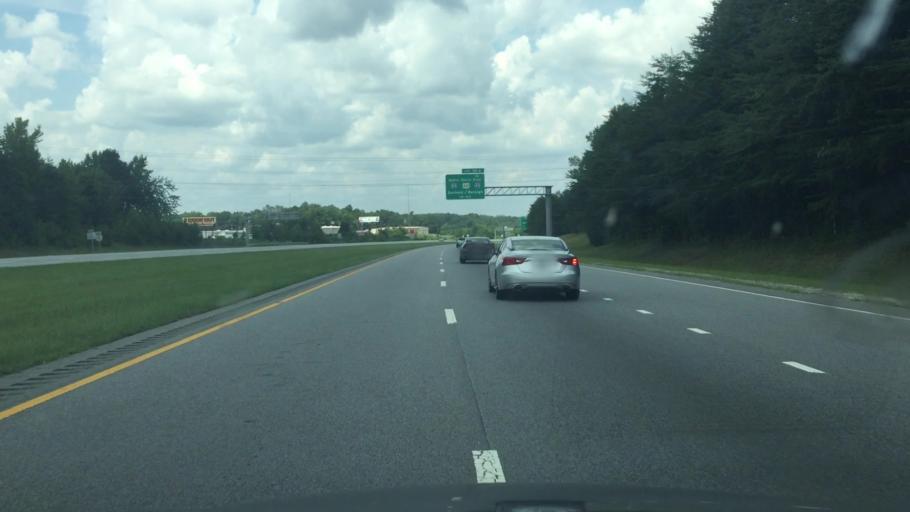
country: US
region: North Carolina
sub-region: Guilford County
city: Pleasant Garden
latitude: 35.9928
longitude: -79.8273
